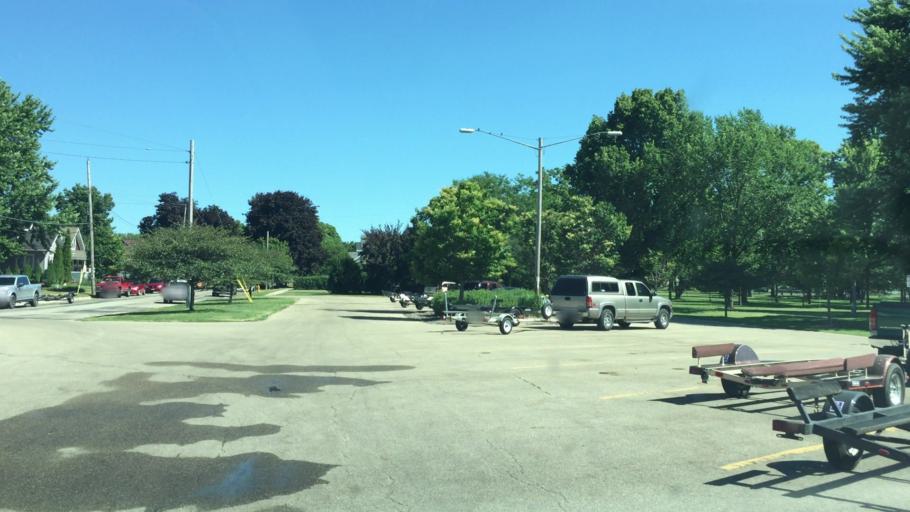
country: US
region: Wisconsin
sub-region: Winnebago County
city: Neenah
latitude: 44.1853
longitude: -88.4495
